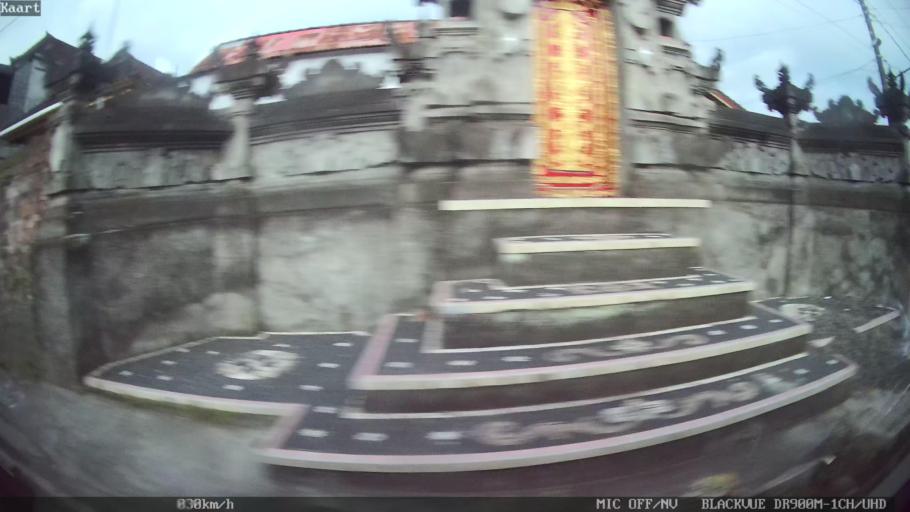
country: ID
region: Bali
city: Banjar Tebongkang
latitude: -8.5249
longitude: 115.2487
